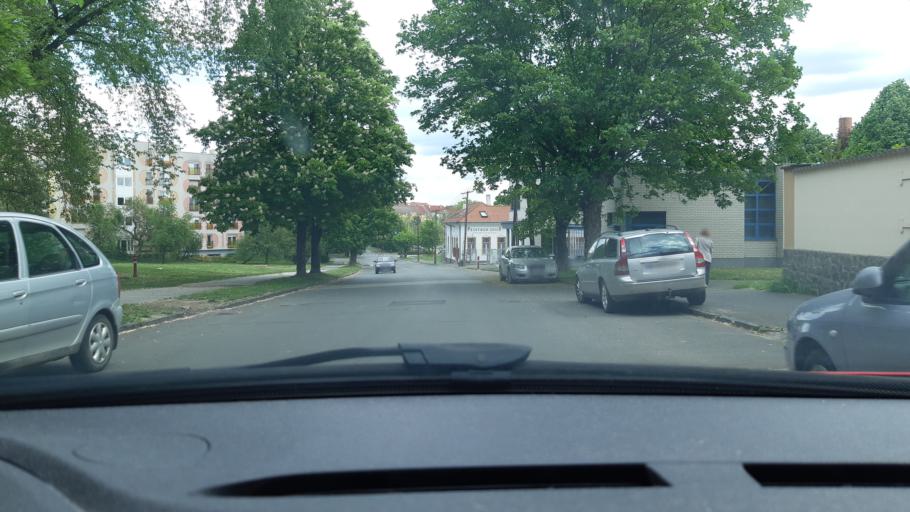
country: HU
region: Somogy
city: Kaposvar
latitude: 46.3627
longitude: 17.7791
